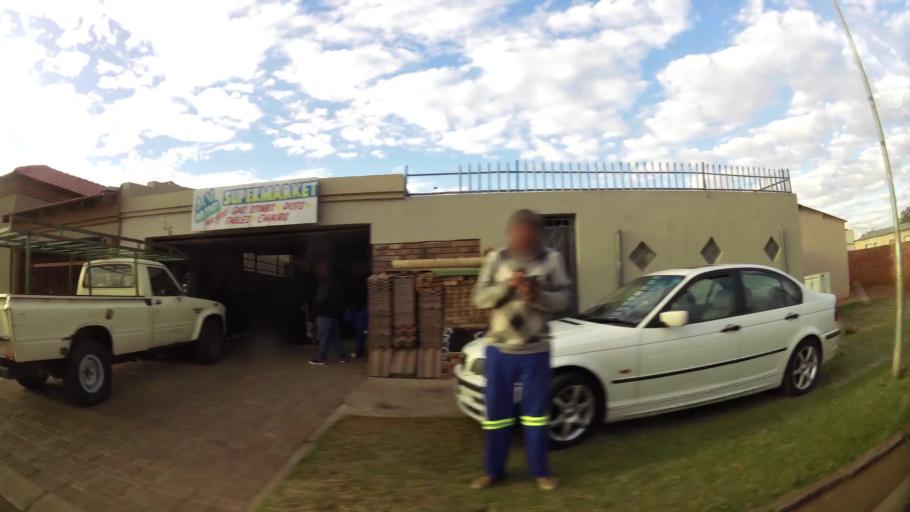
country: ZA
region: Gauteng
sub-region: City of Tshwane Metropolitan Municipality
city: Pretoria
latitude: -25.7021
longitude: 28.3173
